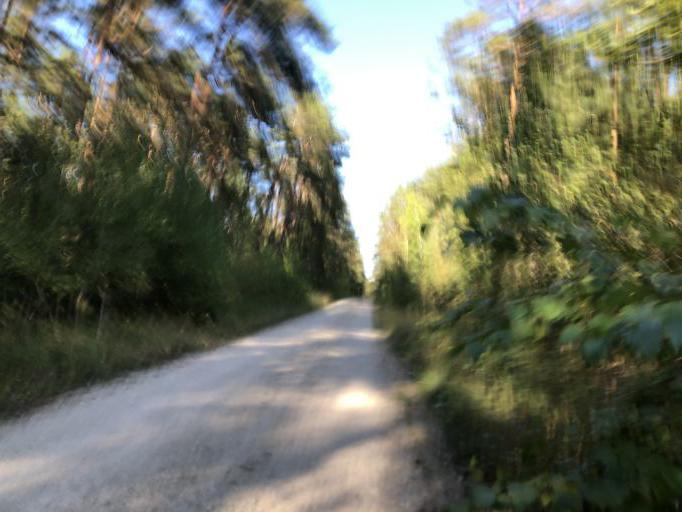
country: DE
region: Bavaria
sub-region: Regierungsbezirk Mittelfranken
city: Buckenhof
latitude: 49.5423
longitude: 11.0558
